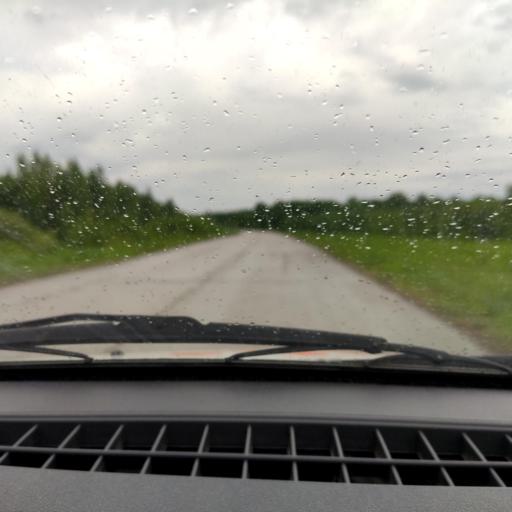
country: RU
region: Bashkortostan
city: Urman
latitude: 54.8563
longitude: 56.8293
